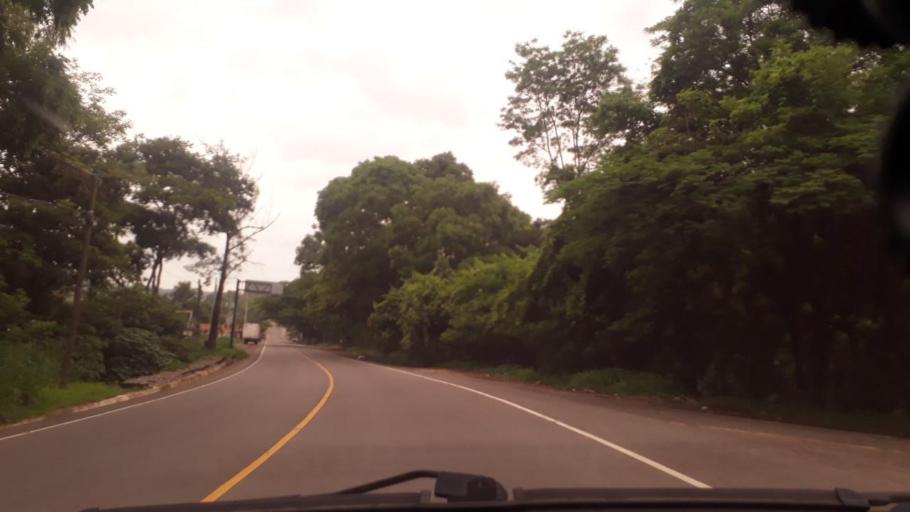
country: GT
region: Chiquimula
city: Quezaltepeque
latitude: 14.6360
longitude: -89.4489
